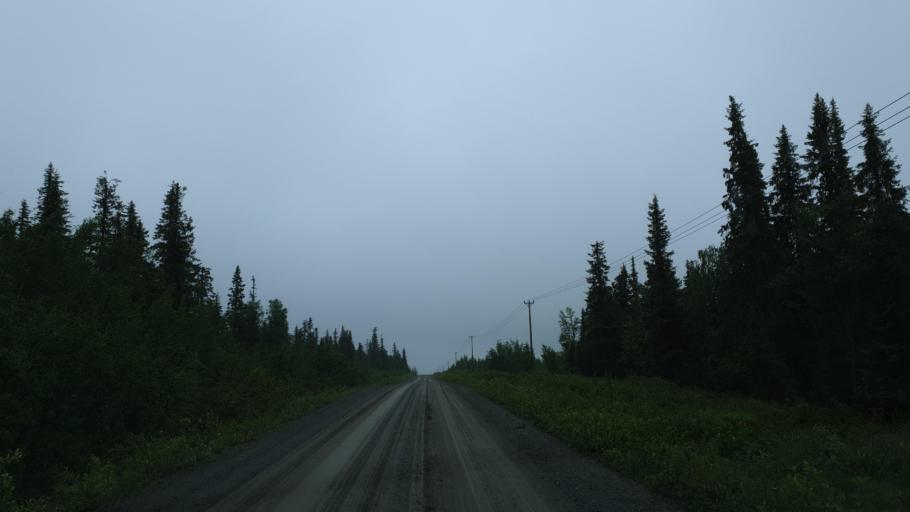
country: SE
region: Vaesterbotten
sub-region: Vilhelmina Kommun
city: Sjoberg
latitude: 65.3165
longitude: 15.9530
